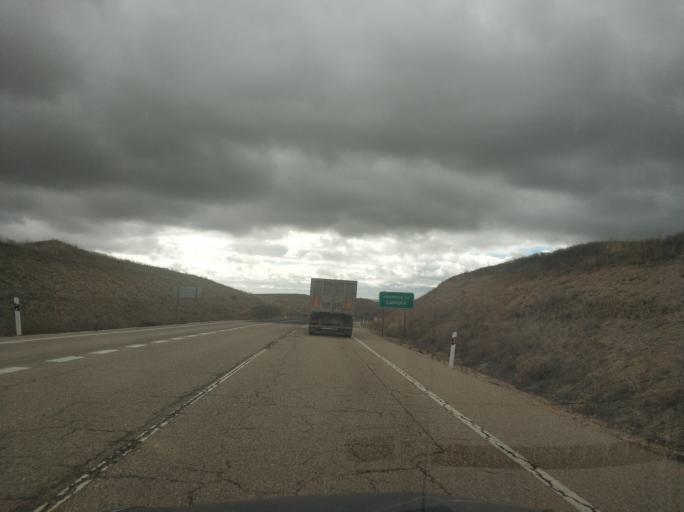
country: ES
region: Castille and Leon
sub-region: Provincia de Zamora
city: Castrillo de la Guarena
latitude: 41.2415
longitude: -5.2961
